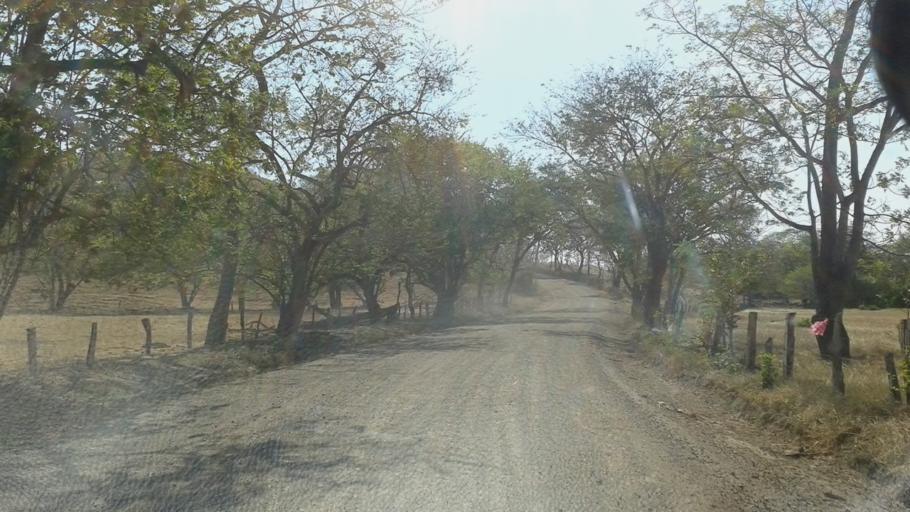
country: CR
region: Guanacaste
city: Santa Cruz
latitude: 10.1849
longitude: -85.7701
